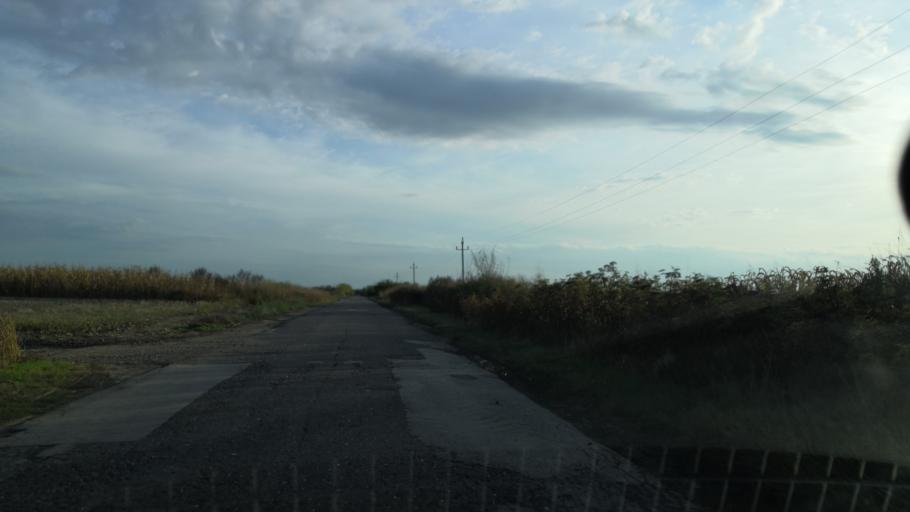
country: RS
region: Autonomna Pokrajina Vojvodina
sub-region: Sremski Okrug
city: Stara Pazova
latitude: 45.0057
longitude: 20.1662
